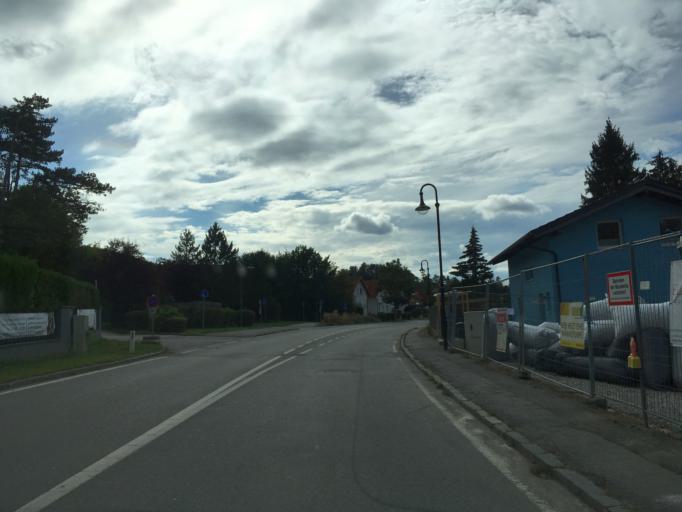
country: AT
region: Lower Austria
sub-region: Politischer Bezirk Modling
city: Gaaden
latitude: 48.0620
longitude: 16.2160
